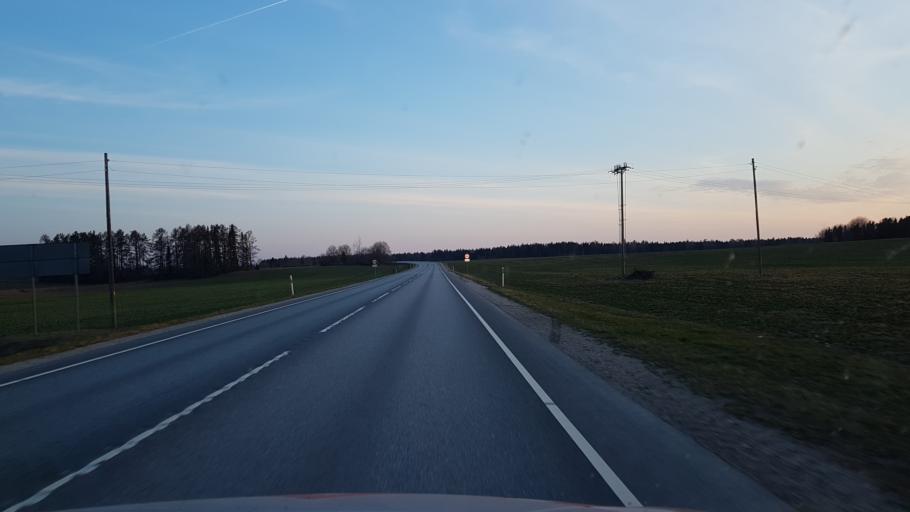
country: EE
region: Laeaene-Virumaa
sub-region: Kadrina vald
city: Kadrina
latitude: 59.2975
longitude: 26.0577
